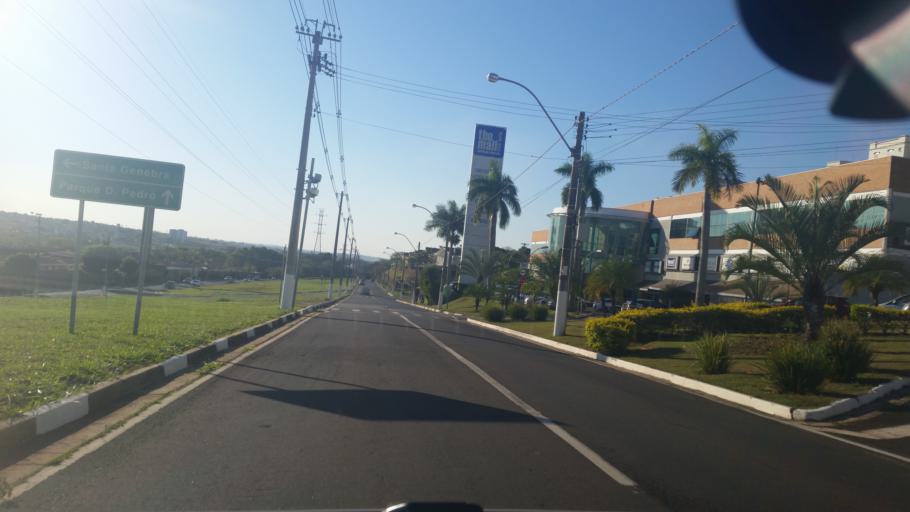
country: BR
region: Sao Paulo
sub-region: Campinas
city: Campinas
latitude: -22.8566
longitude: -47.0558
